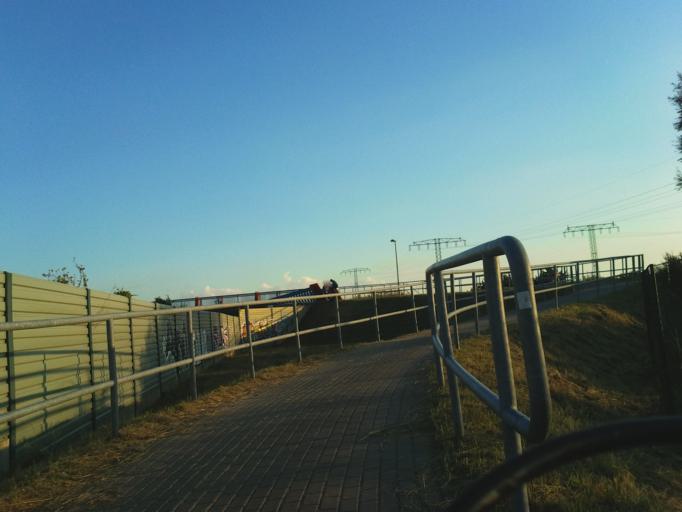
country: DE
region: Mecklenburg-Vorpommern
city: Kritzmow
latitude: 54.0881
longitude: 12.0674
